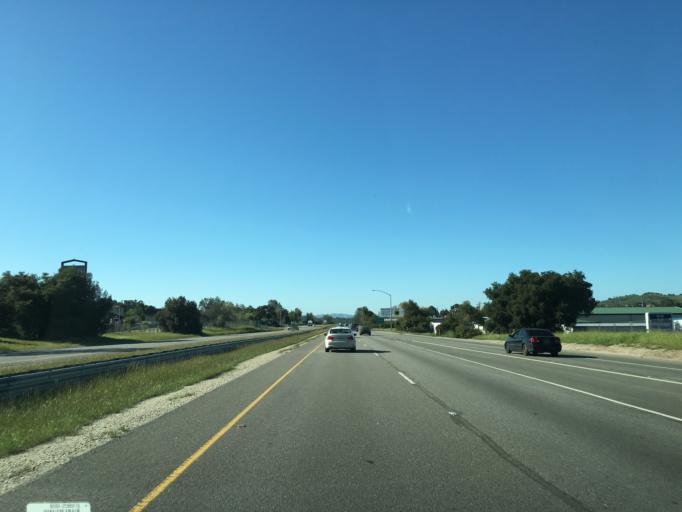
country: US
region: California
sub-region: San Luis Obispo County
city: Atascadero
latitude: 35.4672
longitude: -120.6522
